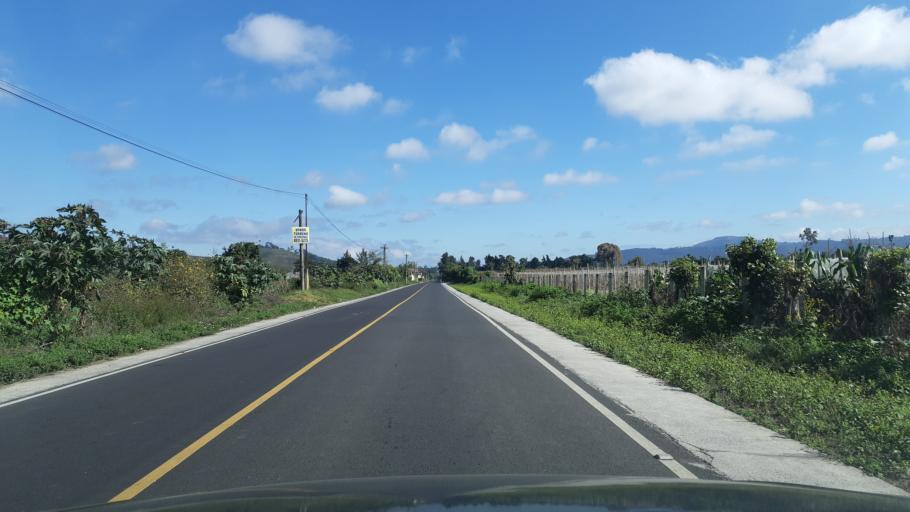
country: GT
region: Chimaltenango
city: San Andres Itzapa
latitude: 14.6310
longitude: -90.8298
